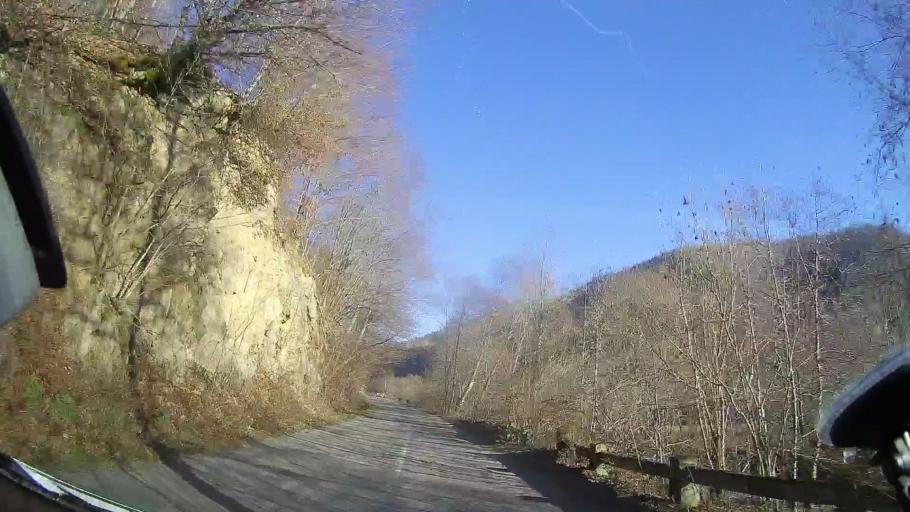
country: RO
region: Cluj
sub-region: Comuna Sacueu
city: Sacuieu
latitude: 46.8541
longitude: 22.8629
